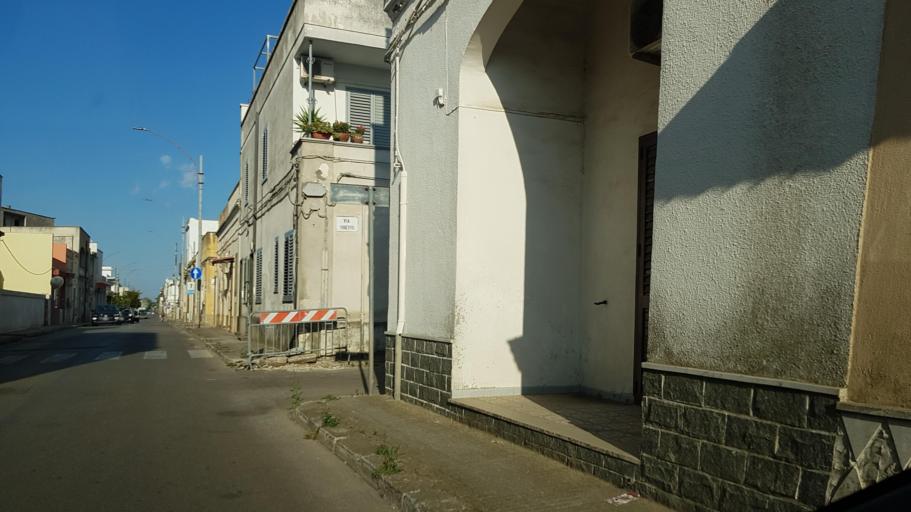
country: IT
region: Apulia
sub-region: Provincia di Lecce
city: Miggiano
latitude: 39.9651
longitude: 18.3067
